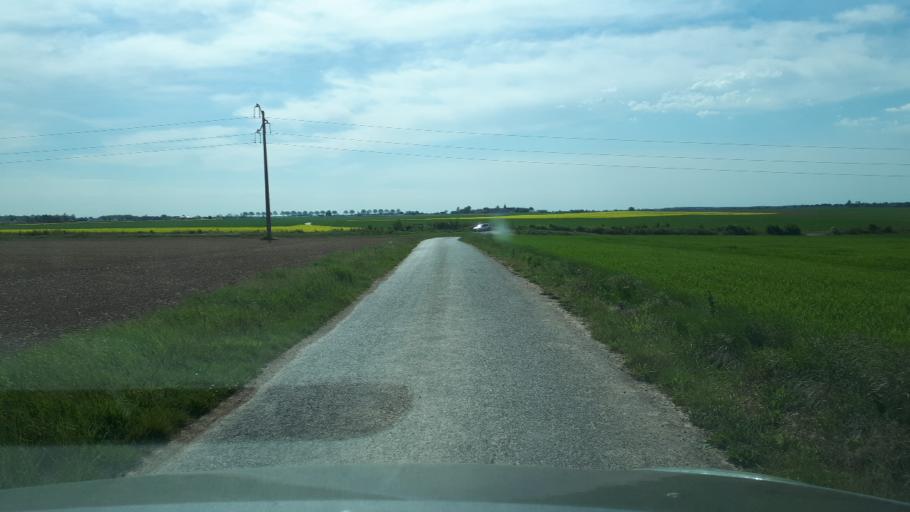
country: FR
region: Centre
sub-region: Departement du Loir-et-Cher
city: Naveil
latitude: 47.7650
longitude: 1.0156
